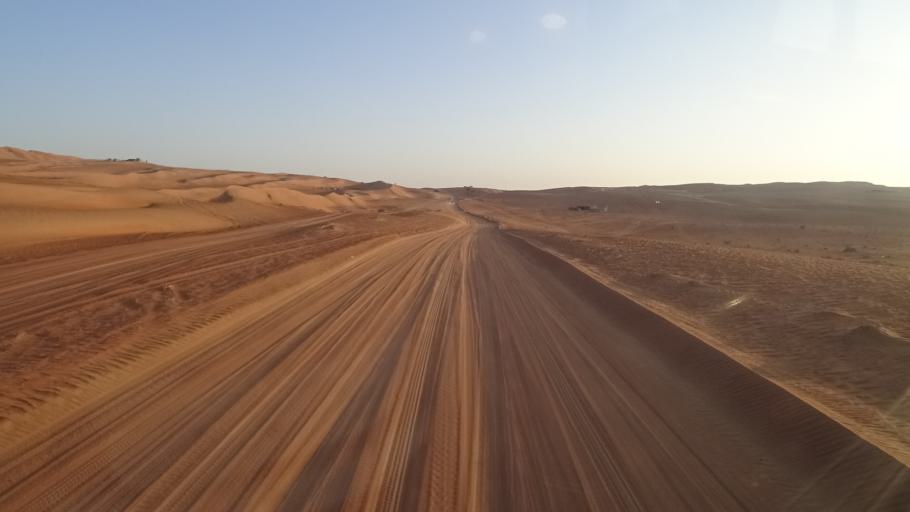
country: OM
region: Ash Sharqiyah
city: Badiyah
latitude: 22.4870
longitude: 58.7291
